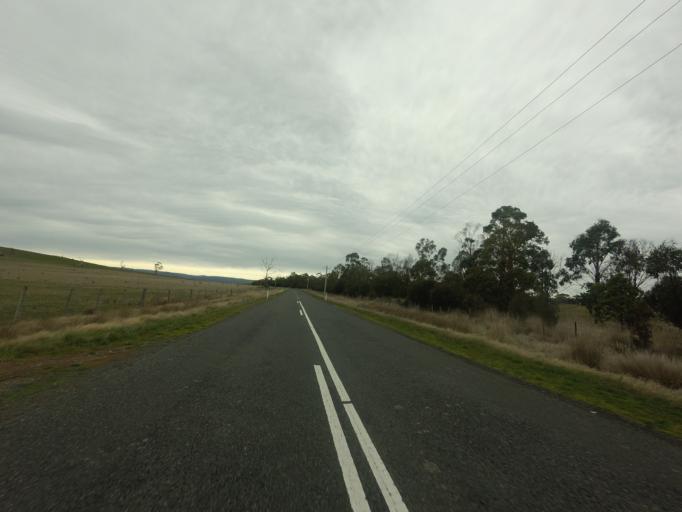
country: AU
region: Tasmania
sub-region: Derwent Valley
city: New Norfolk
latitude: -42.4140
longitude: 147.0063
